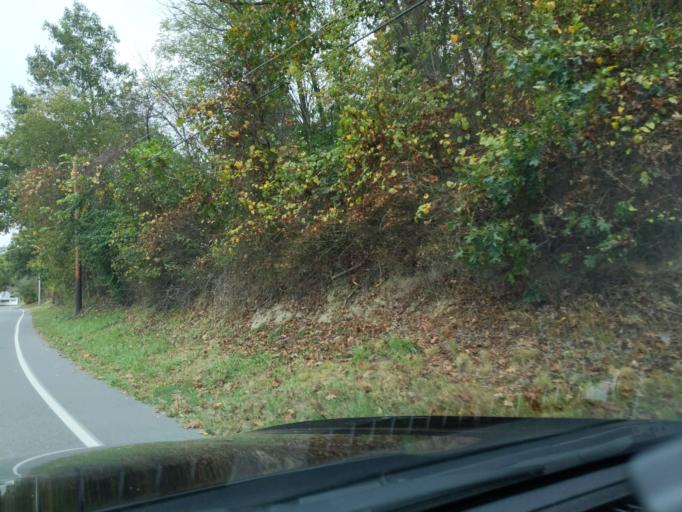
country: US
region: Pennsylvania
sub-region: Blair County
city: Altoona
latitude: 40.4911
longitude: -78.4459
